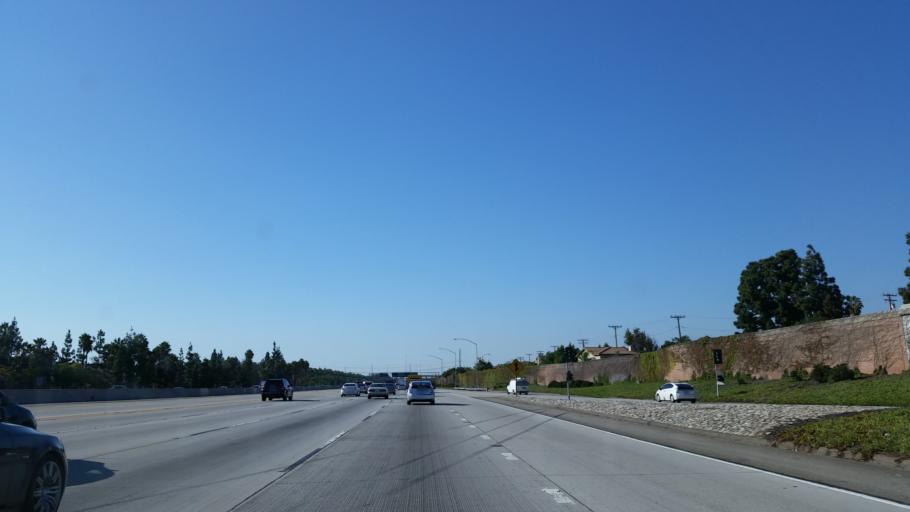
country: US
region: California
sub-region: Orange County
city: Buena Park
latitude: 33.8474
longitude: -117.9625
